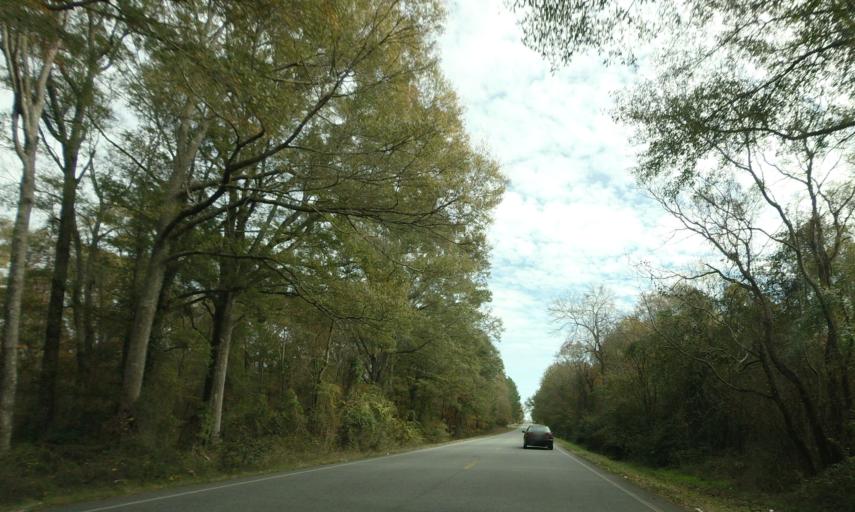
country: US
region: Georgia
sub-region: Dodge County
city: Chester
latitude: 32.4101
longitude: -83.2397
